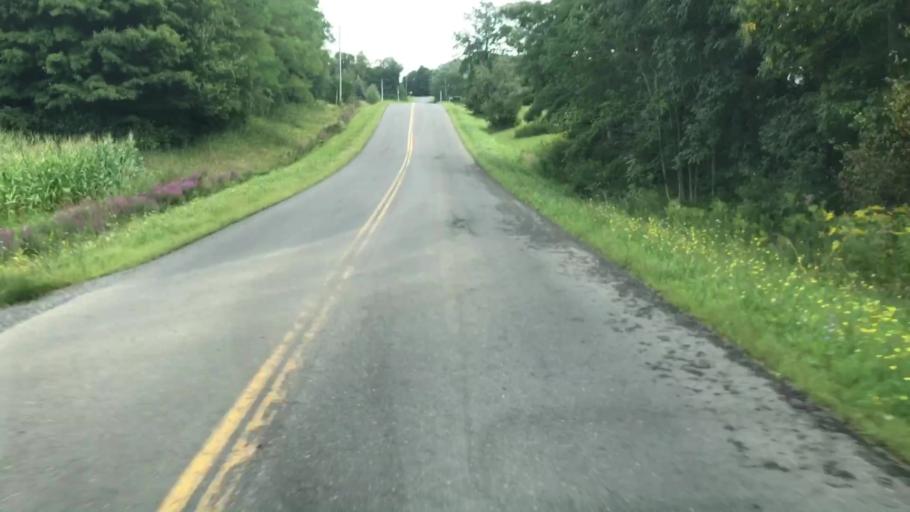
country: US
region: New York
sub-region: Cayuga County
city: Melrose Park
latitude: 42.9204
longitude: -76.4958
